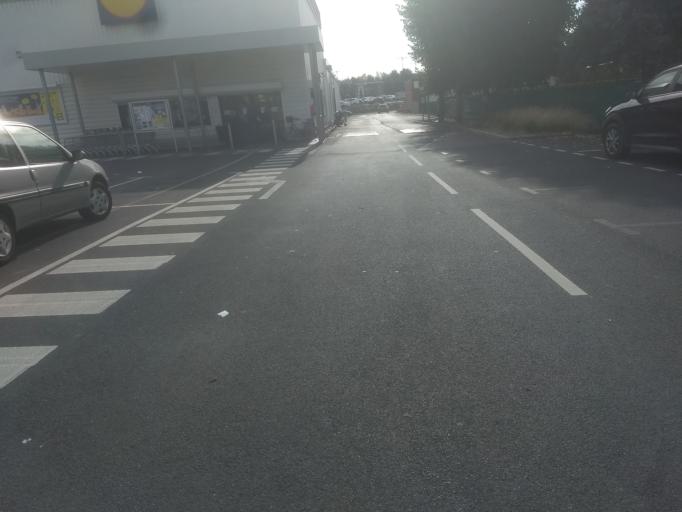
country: FR
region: Nord-Pas-de-Calais
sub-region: Departement du Pas-de-Calais
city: Dainville
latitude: 50.2843
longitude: 2.7374
